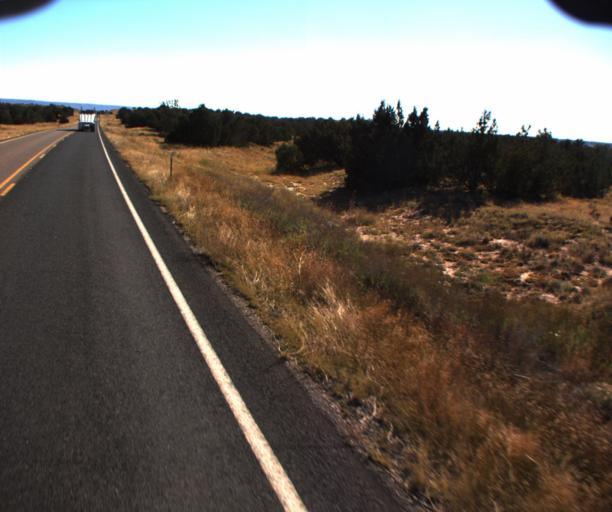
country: US
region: Arizona
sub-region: Apache County
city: Ganado
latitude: 35.4465
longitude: -109.5220
